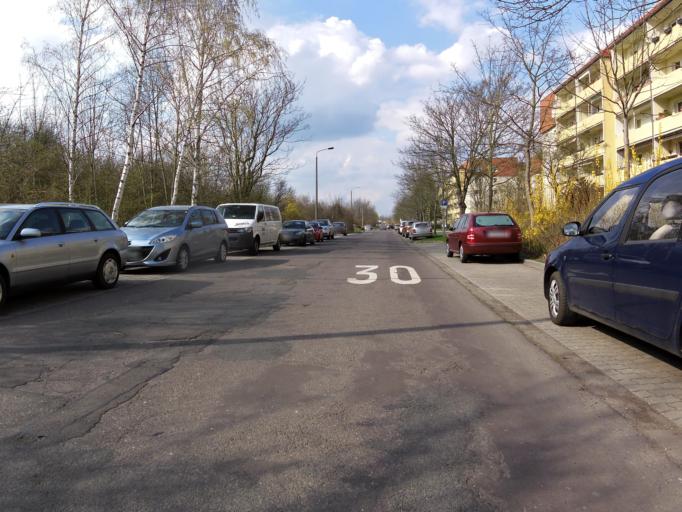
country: DE
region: Saxony
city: Markranstadt
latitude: 51.3131
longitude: 12.2811
